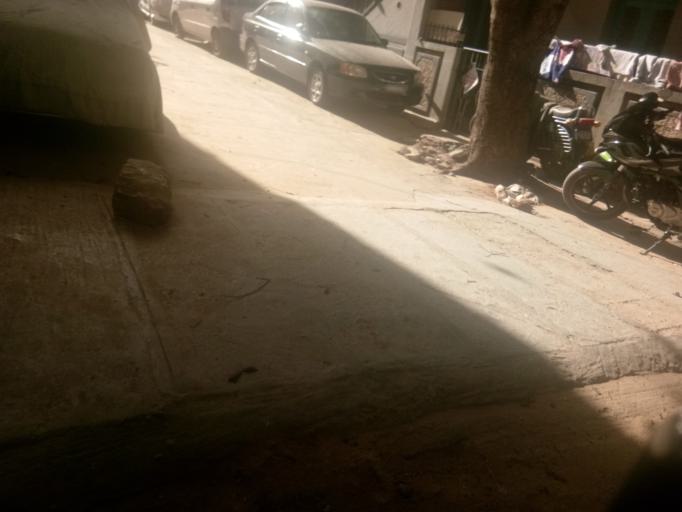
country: IN
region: Karnataka
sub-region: Bangalore Urban
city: Bangalore
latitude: 13.0047
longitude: 77.5984
